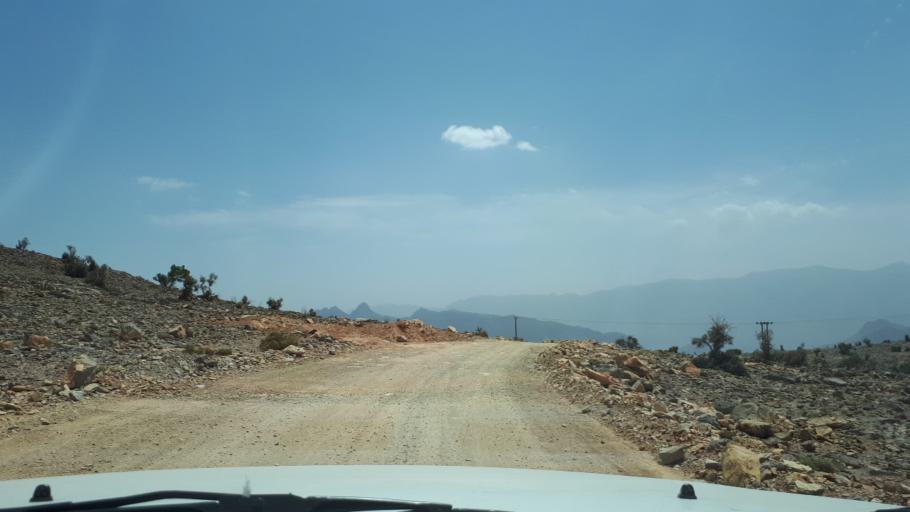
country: OM
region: Muhafazat ad Dakhiliyah
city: Bahla'
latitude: 23.1994
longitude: 57.2014
